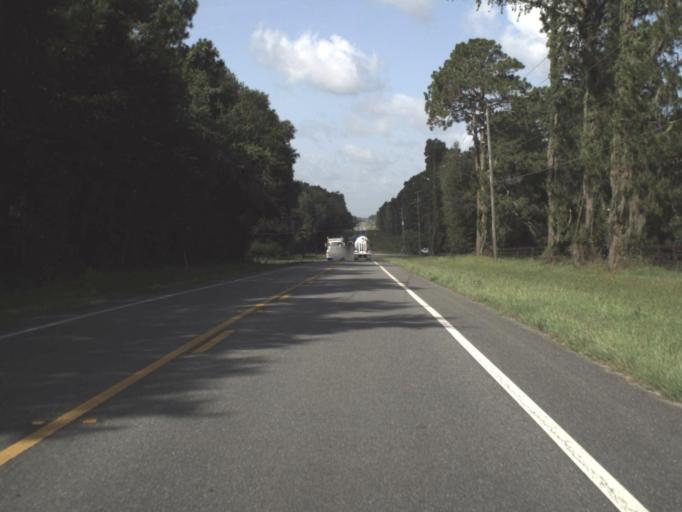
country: US
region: Florida
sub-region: Columbia County
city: Lake City
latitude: 30.1271
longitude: -82.7194
